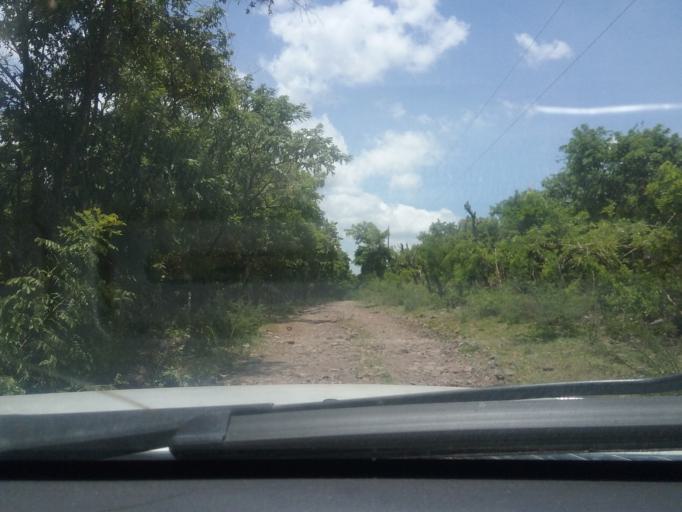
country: NI
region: Matagalpa
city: Terrabona
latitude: 12.6598
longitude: -85.9884
